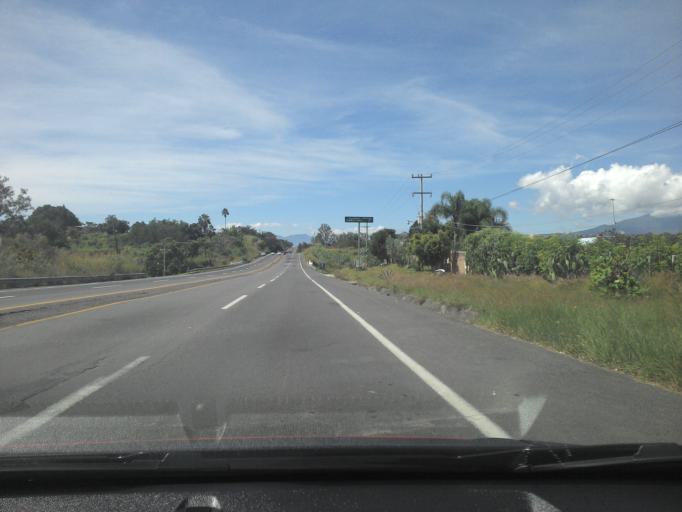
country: MX
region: Jalisco
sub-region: Tala
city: Los Ruisenores
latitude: 20.7198
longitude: -103.6288
